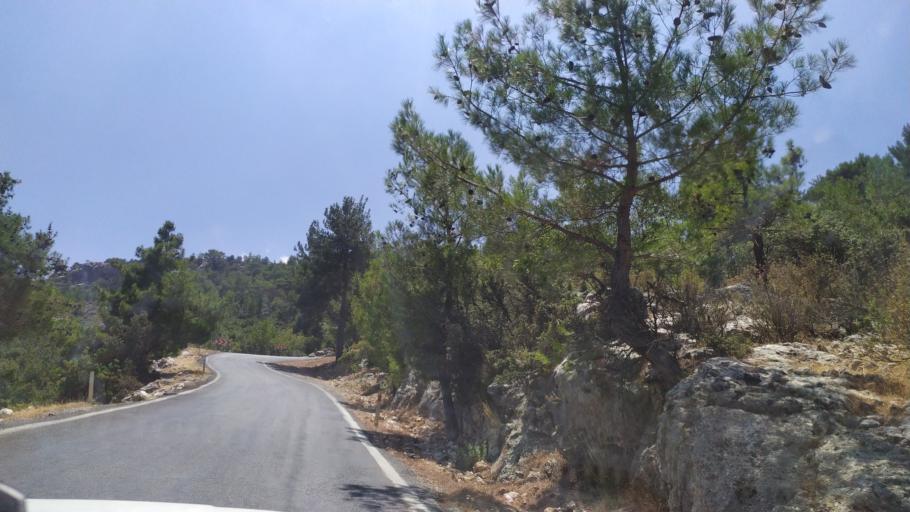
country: TR
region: Mersin
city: Gulnar
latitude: 36.2753
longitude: 33.3807
